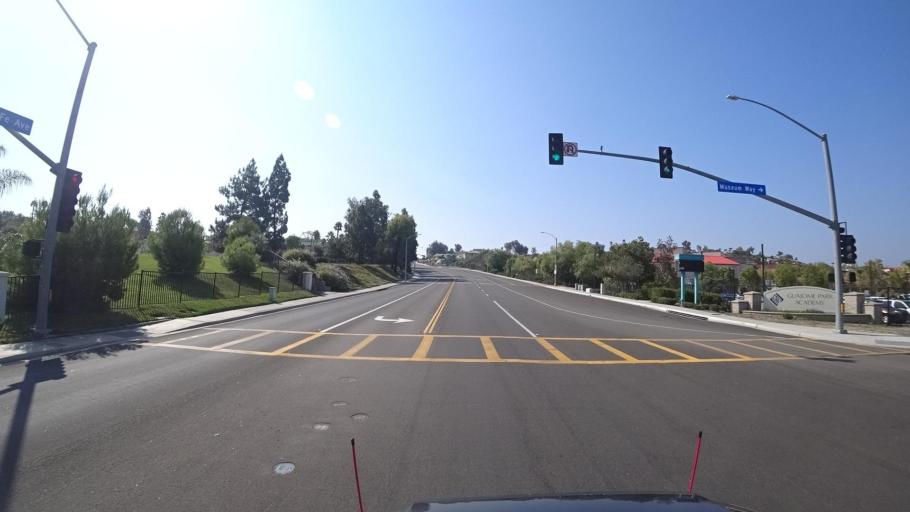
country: US
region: California
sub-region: San Diego County
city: Vista
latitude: 33.2309
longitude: -117.2490
